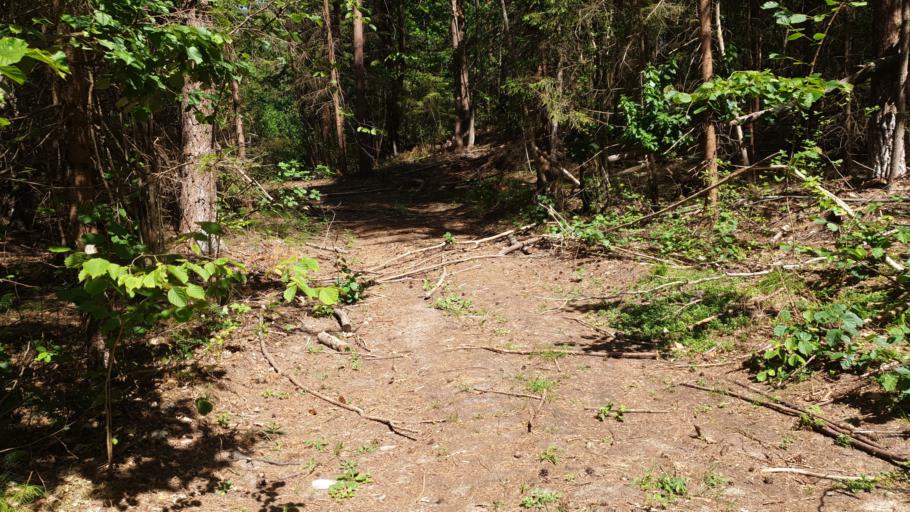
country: LT
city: Grigiskes
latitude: 54.7805
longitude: 24.9926
